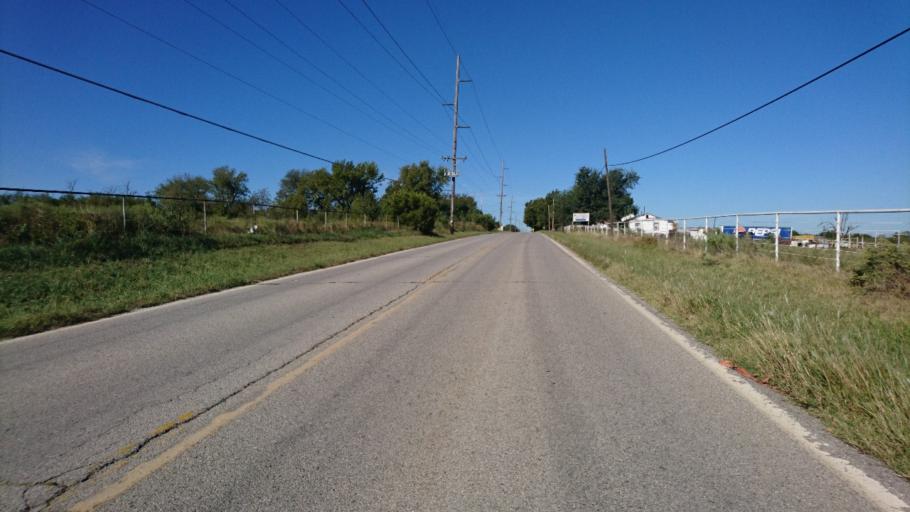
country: US
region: Oklahoma
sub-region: Rogers County
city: Catoosa
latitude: 36.1480
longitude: -95.7900
